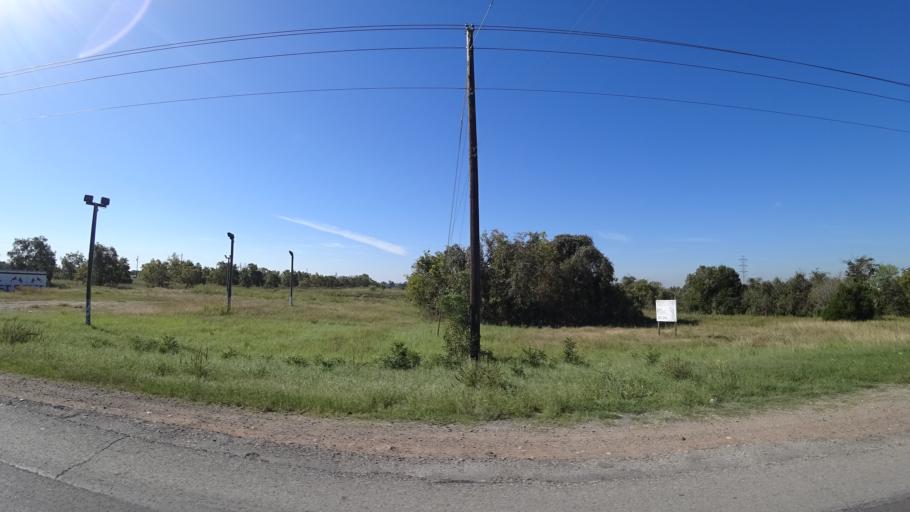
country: US
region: Texas
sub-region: Travis County
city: Hornsby Bend
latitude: 30.2516
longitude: -97.5995
